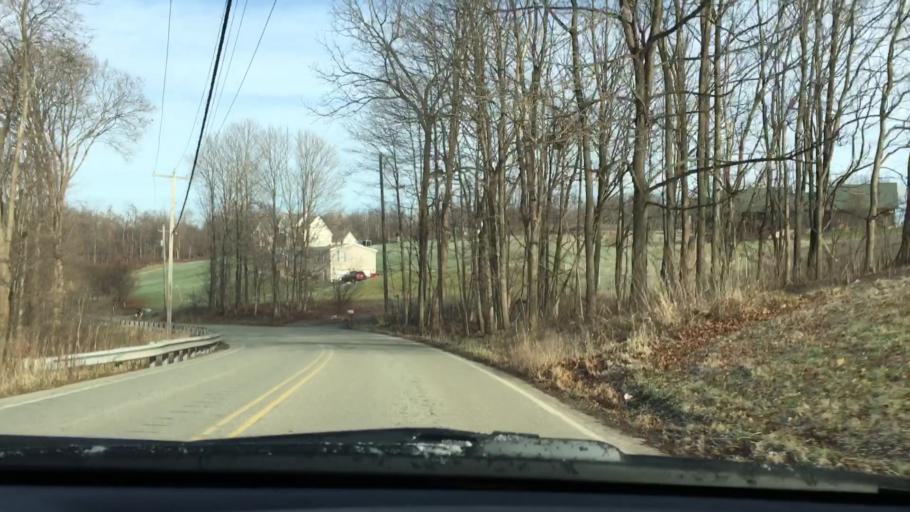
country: US
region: Pennsylvania
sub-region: Westmoreland County
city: Collinsburg
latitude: 40.2630
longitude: -79.7402
